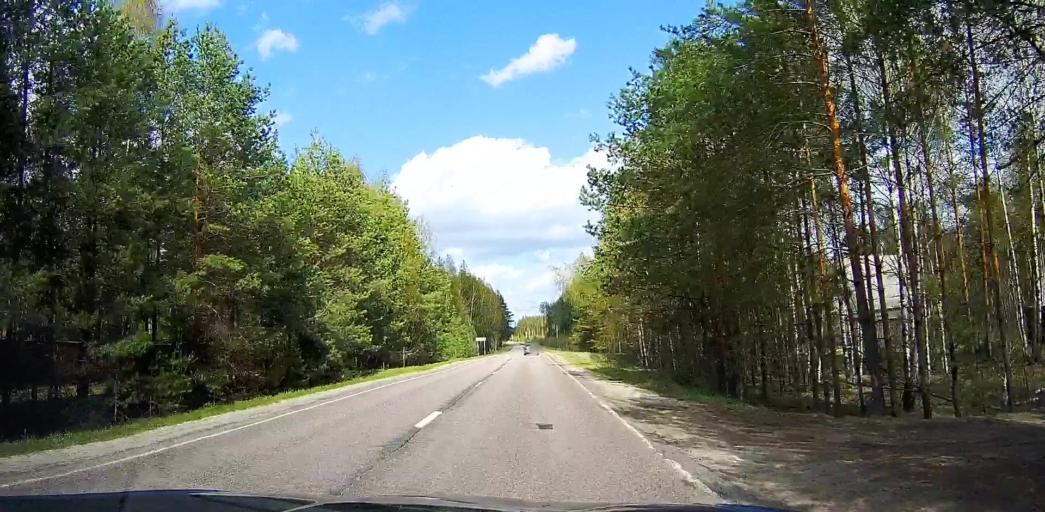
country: RU
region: Moskovskaya
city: Davydovo
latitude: 55.5909
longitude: 38.8328
